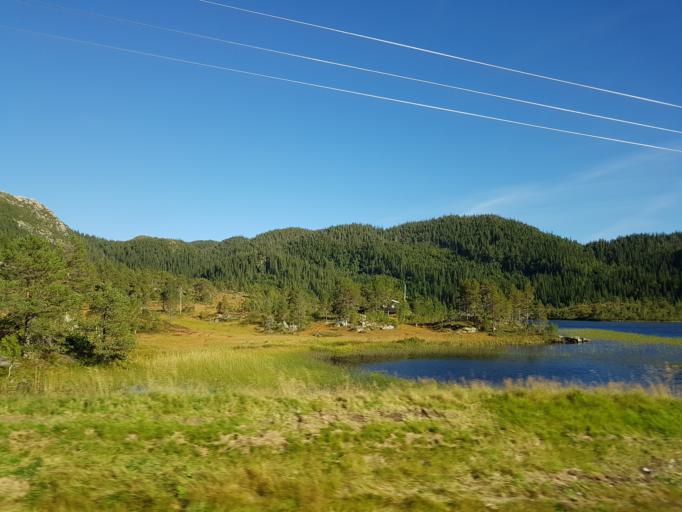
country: NO
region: Sor-Trondelag
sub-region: Afjord
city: A i Afjord
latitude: 63.6999
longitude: 10.2385
